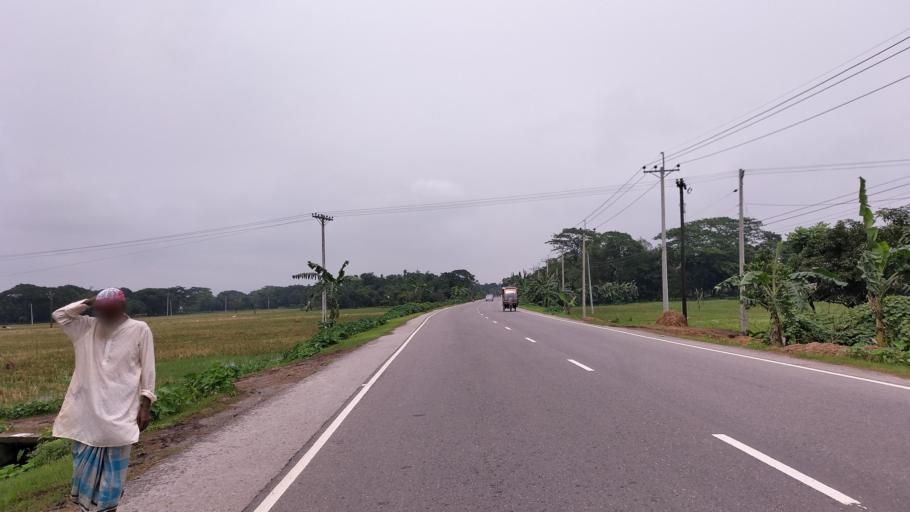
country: BD
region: Dhaka
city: Netrakona
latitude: 24.8509
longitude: 90.6309
